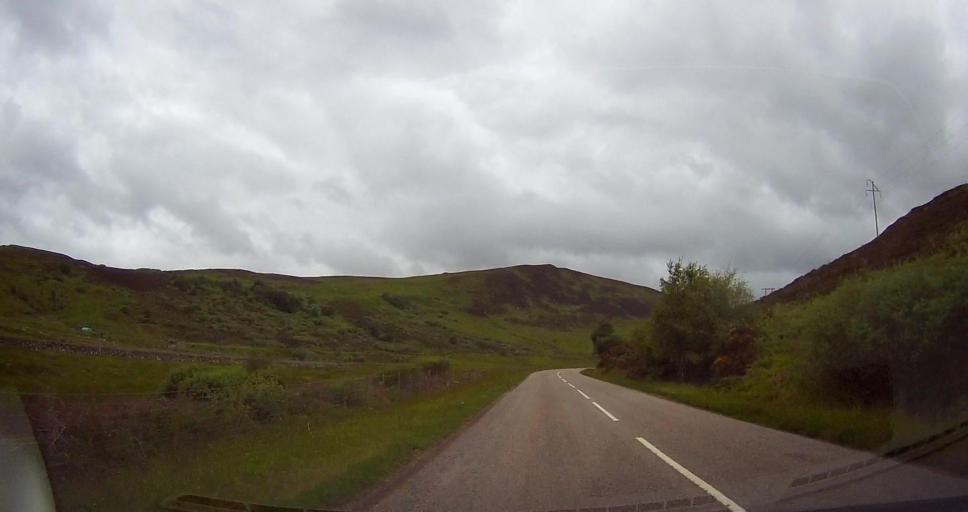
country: GB
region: Scotland
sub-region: Highland
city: Dornoch
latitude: 58.0063
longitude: -4.2630
